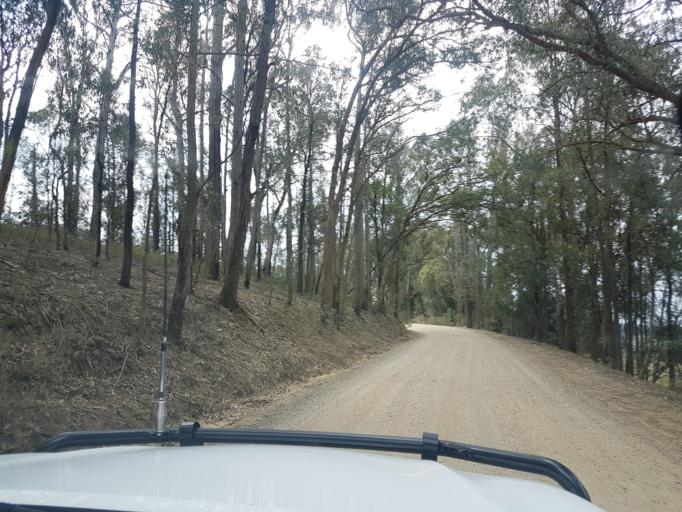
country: AU
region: Victoria
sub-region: East Gippsland
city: Bairnsdale
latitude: -37.6969
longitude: 147.5736
